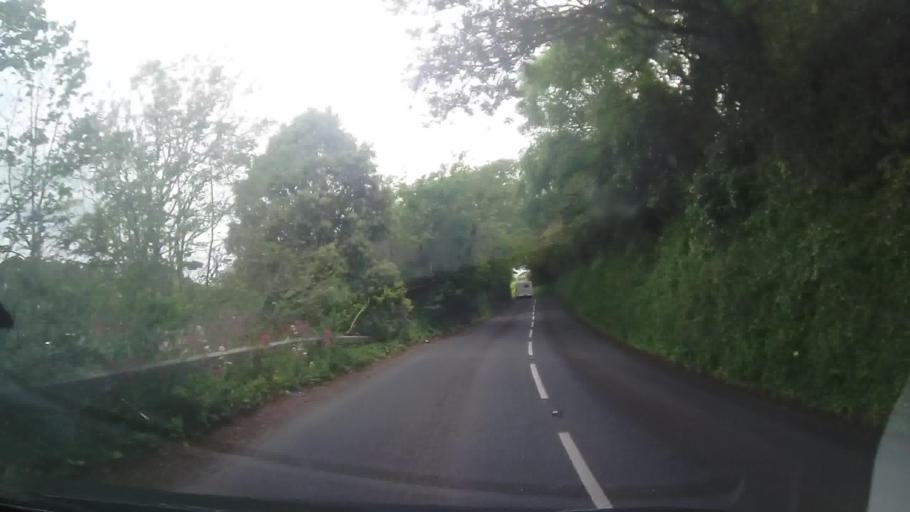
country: GB
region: England
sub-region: Devon
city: Kingsbridge
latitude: 50.2720
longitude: -3.7609
